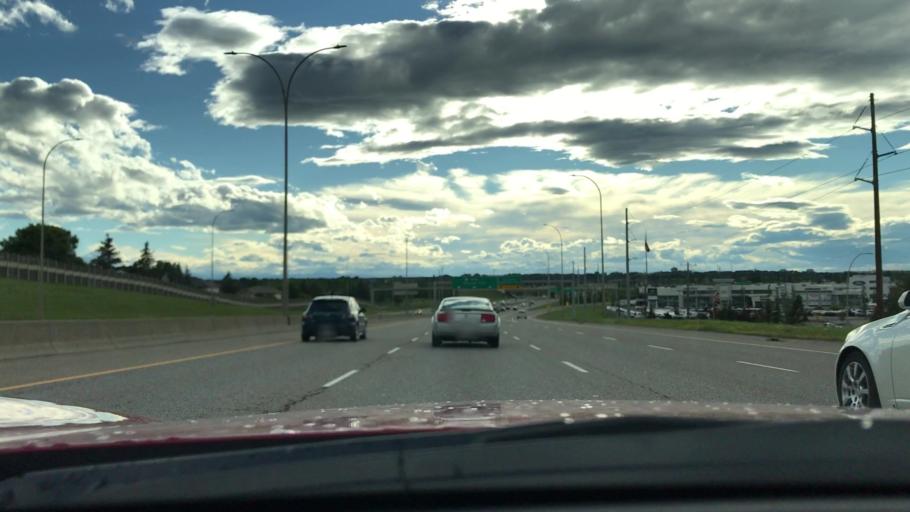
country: CA
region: Alberta
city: Calgary
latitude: 50.9474
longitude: -113.9943
